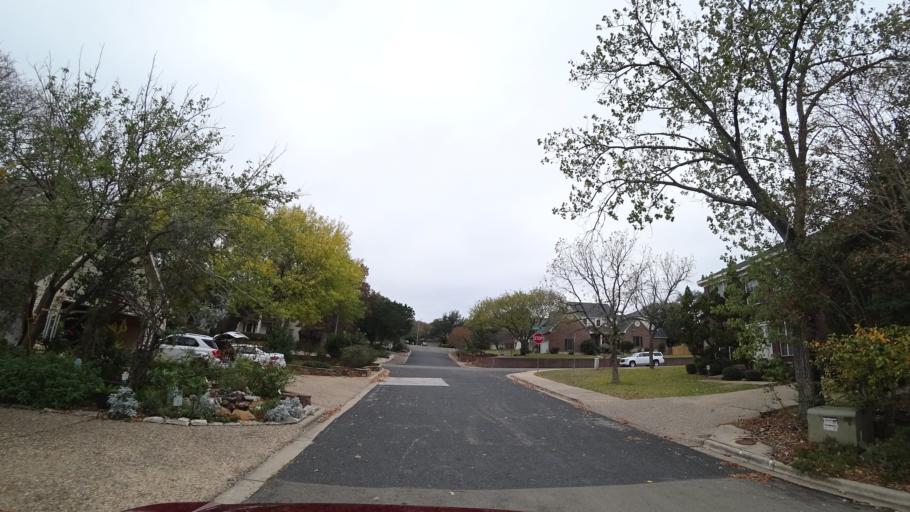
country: US
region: Texas
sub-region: Williamson County
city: Jollyville
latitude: 30.3793
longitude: -97.7973
